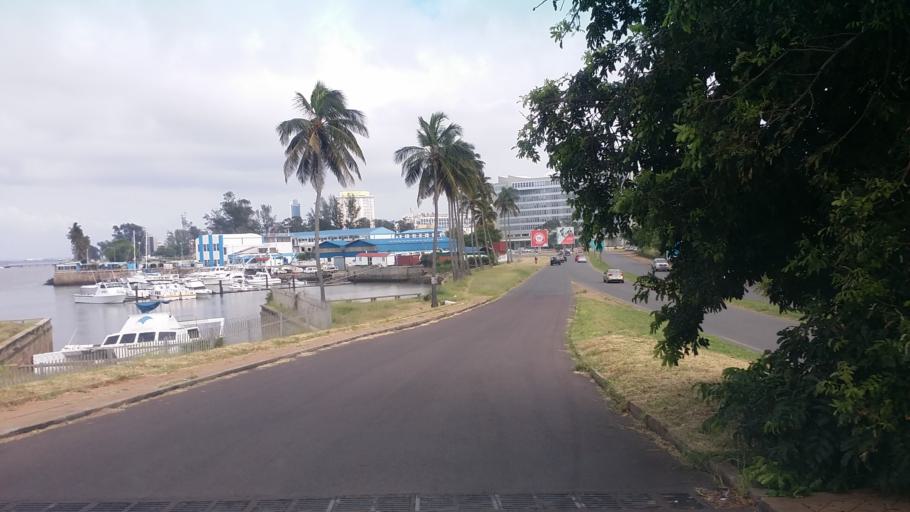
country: MZ
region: Maputo City
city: Maputo
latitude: -25.9831
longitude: 32.5872
